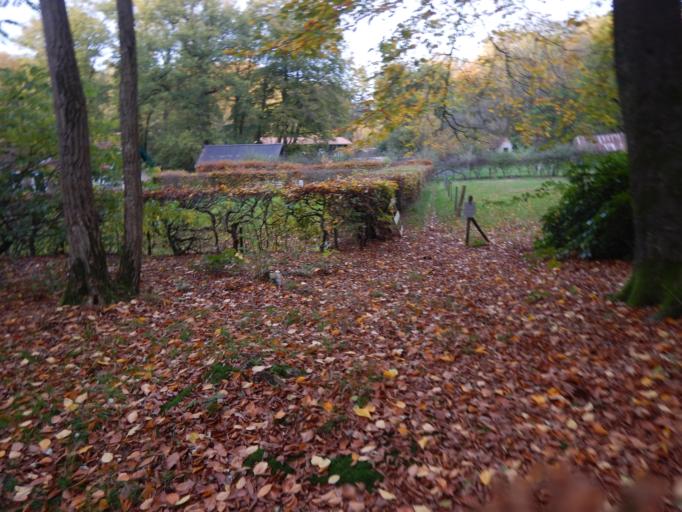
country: NL
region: Gelderland
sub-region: Gemeente Ermelo
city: Ermelo
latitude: 52.2761
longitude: 5.6299
